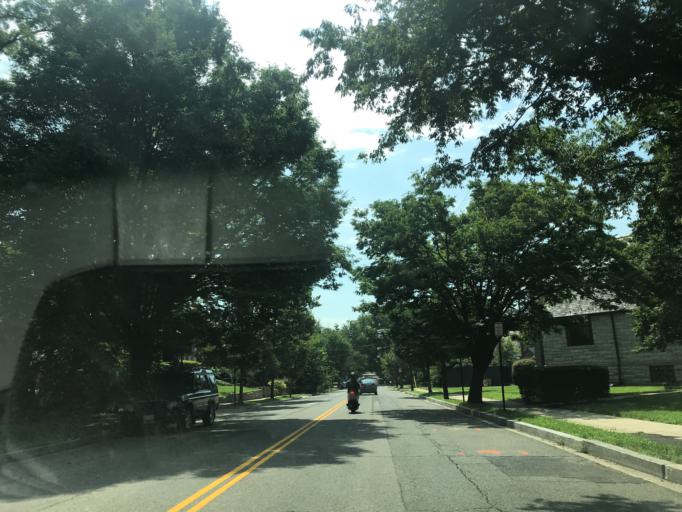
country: US
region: Maryland
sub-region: Montgomery County
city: Friendship Village
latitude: 38.9543
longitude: -77.0882
